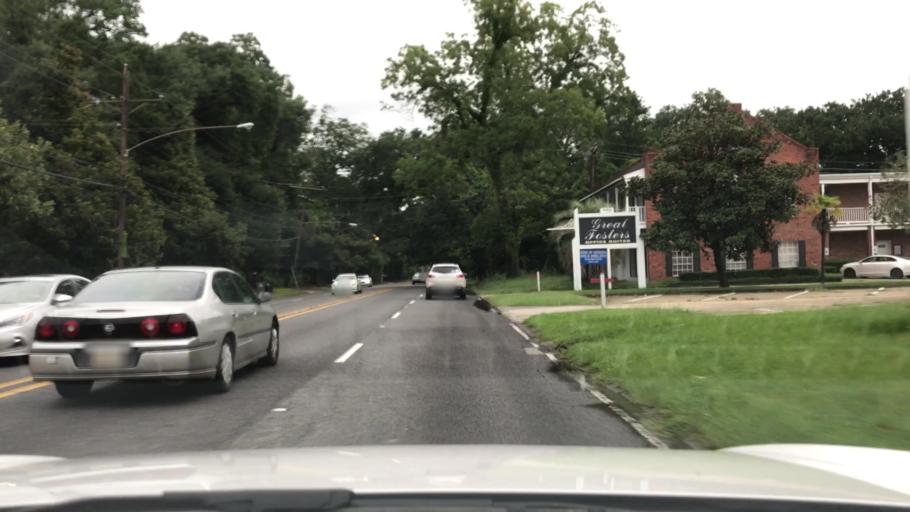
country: US
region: Louisiana
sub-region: East Baton Rouge Parish
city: Baton Rouge
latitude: 30.4551
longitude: -91.1392
